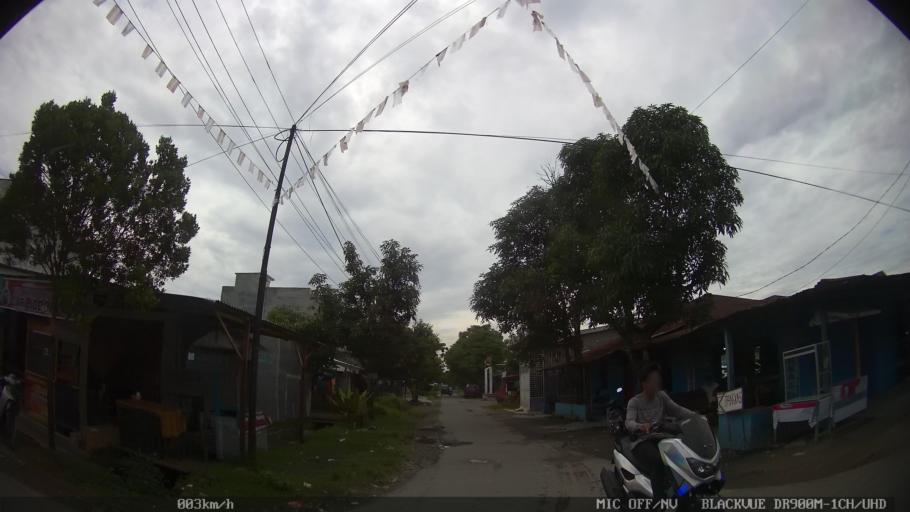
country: ID
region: North Sumatra
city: Sunggal
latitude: 3.5965
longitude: 98.5661
